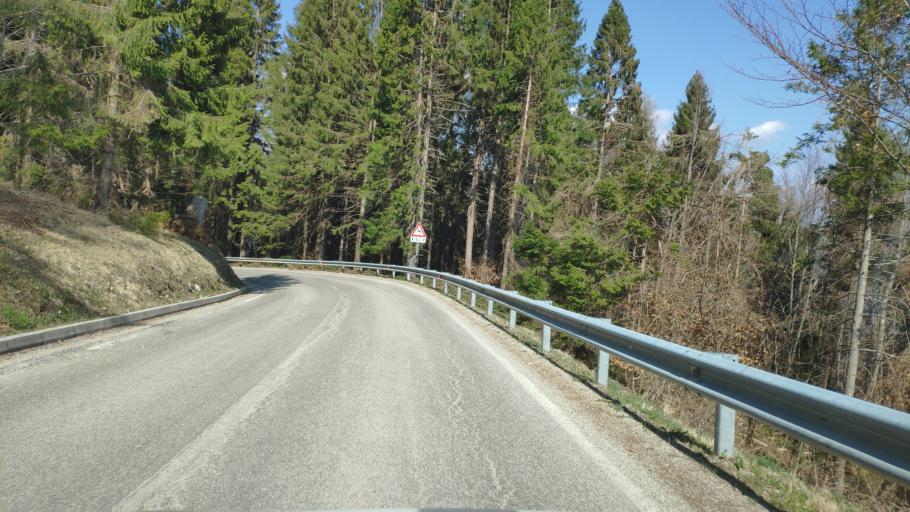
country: IT
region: Veneto
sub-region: Provincia di Vicenza
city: Enego
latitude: 45.9309
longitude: 11.7034
